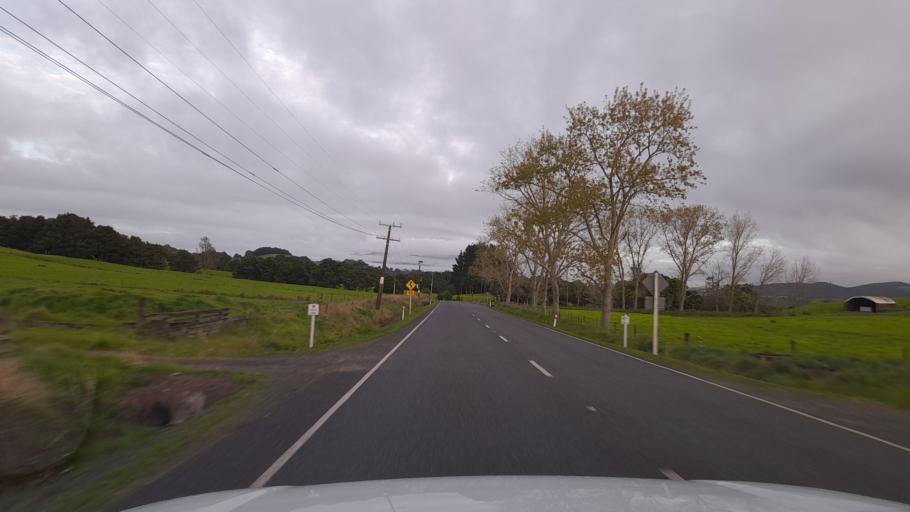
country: NZ
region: Northland
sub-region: Whangarei
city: Maungatapere
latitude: -35.7277
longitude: 174.0453
